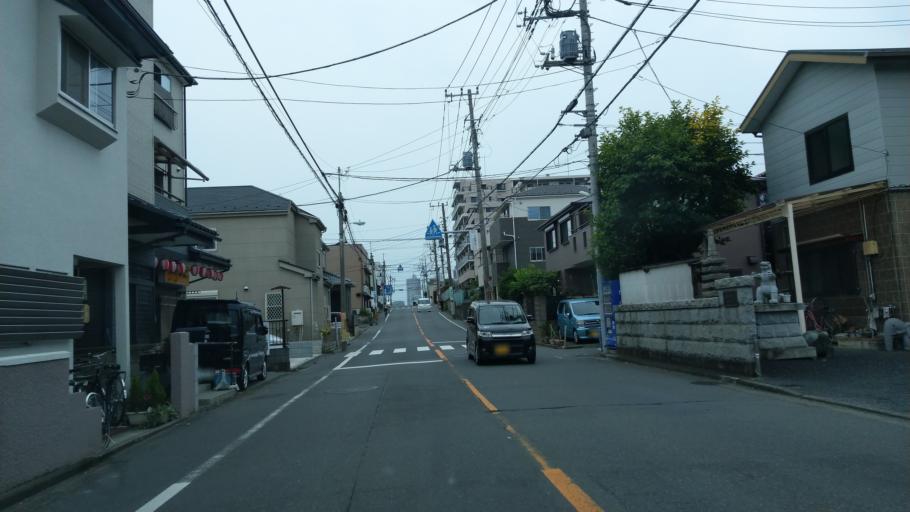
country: JP
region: Saitama
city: Yono
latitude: 35.8652
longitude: 139.6733
